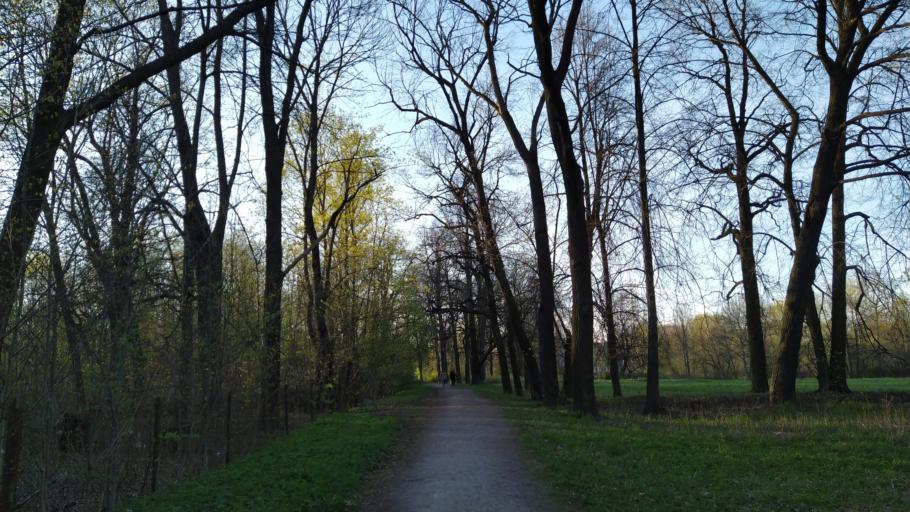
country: RU
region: St.-Petersburg
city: Pushkin
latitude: 59.7098
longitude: 30.4182
